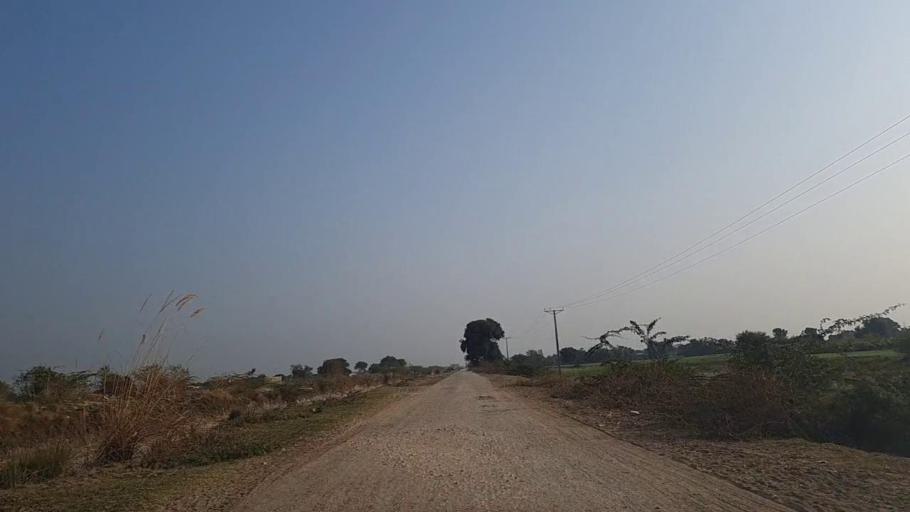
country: PK
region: Sindh
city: Jam Sahib
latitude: 26.2405
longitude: 68.5890
